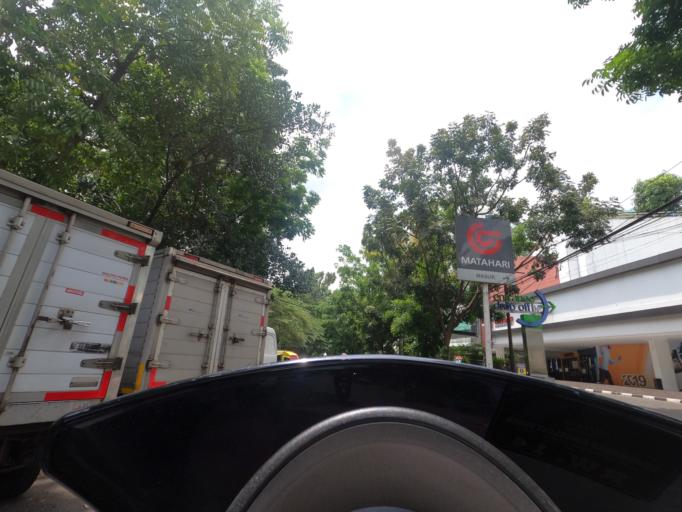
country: ID
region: West Java
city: Bandung
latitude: -6.9083
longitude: 107.6118
